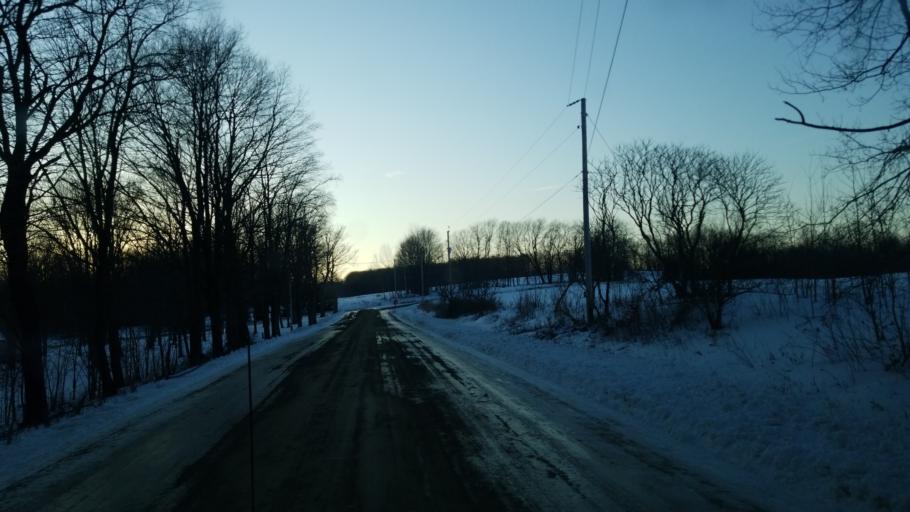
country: US
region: Pennsylvania
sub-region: Tioga County
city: Westfield
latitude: 42.0395
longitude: -77.6175
